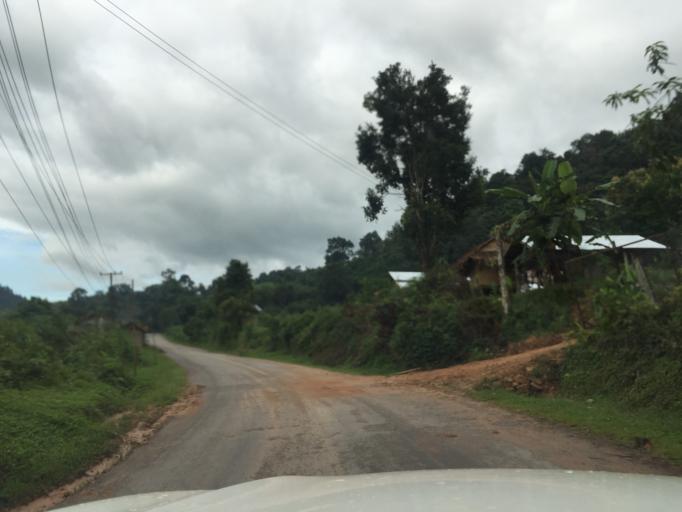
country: LA
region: Oudomxai
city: Muang La
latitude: 20.7879
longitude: 102.0725
